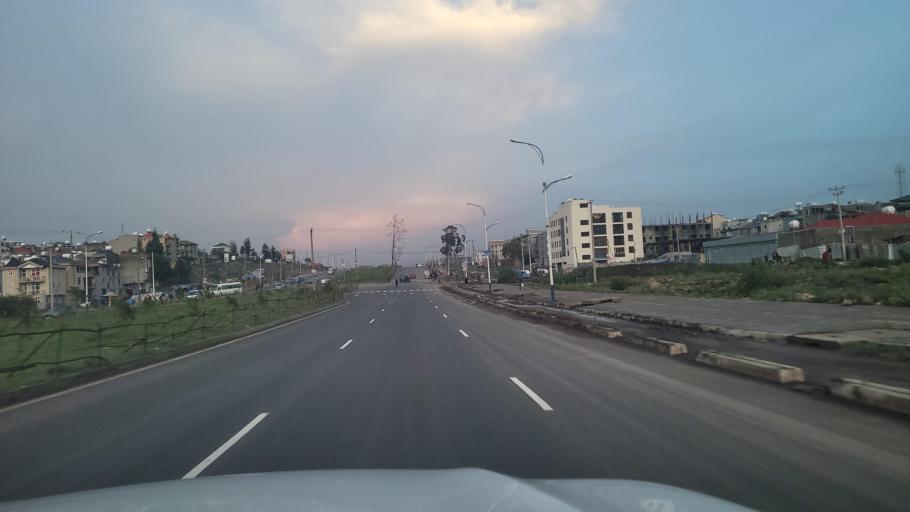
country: ET
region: Adis Abeba
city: Addis Ababa
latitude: 8.9420
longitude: 38.7205
